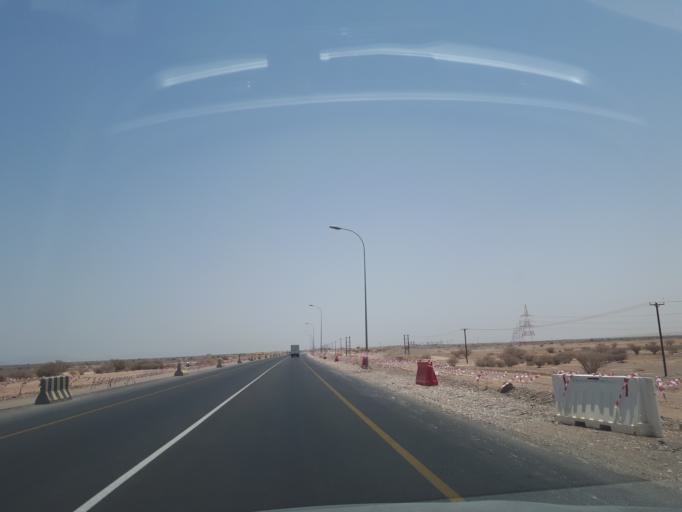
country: OM
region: Ash Sharqiyah
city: Badiyah
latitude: 22.4156
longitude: 59.0522
